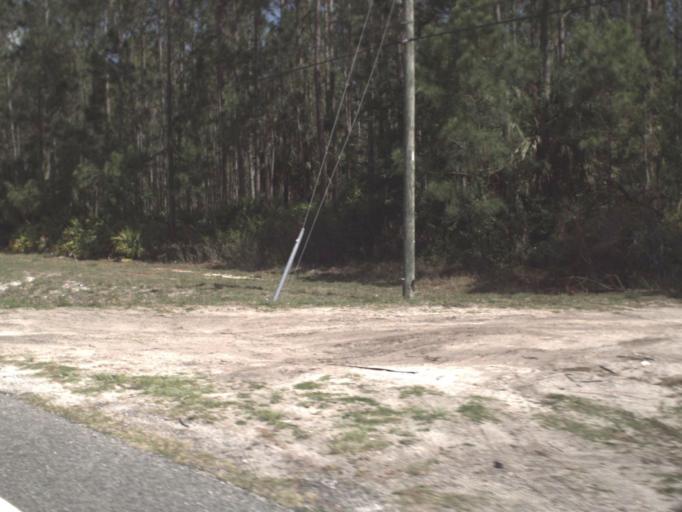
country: US
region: Florida
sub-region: Flagler County
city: Bunnell
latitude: 29.4306
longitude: -81.2282
